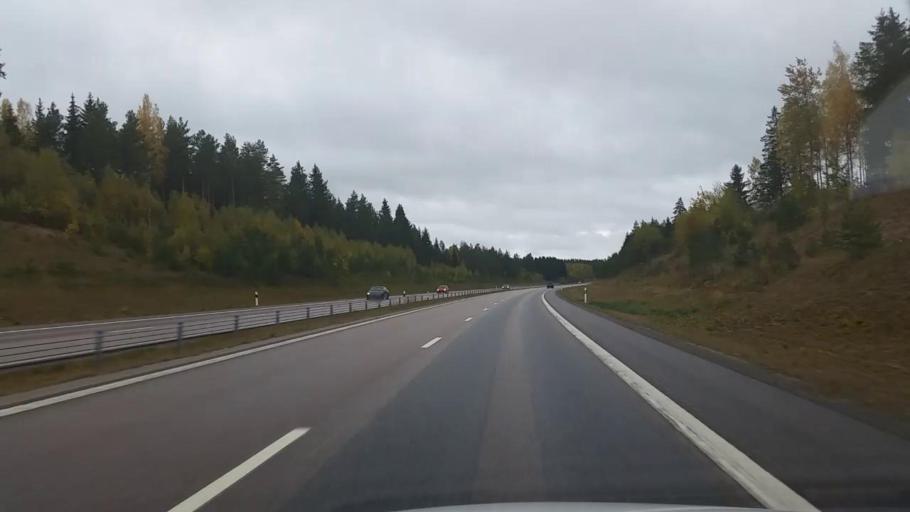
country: SE
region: Uppsala
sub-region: Osthammars Kommun
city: Bjorklinge
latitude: 60.1209
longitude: 17.5473
